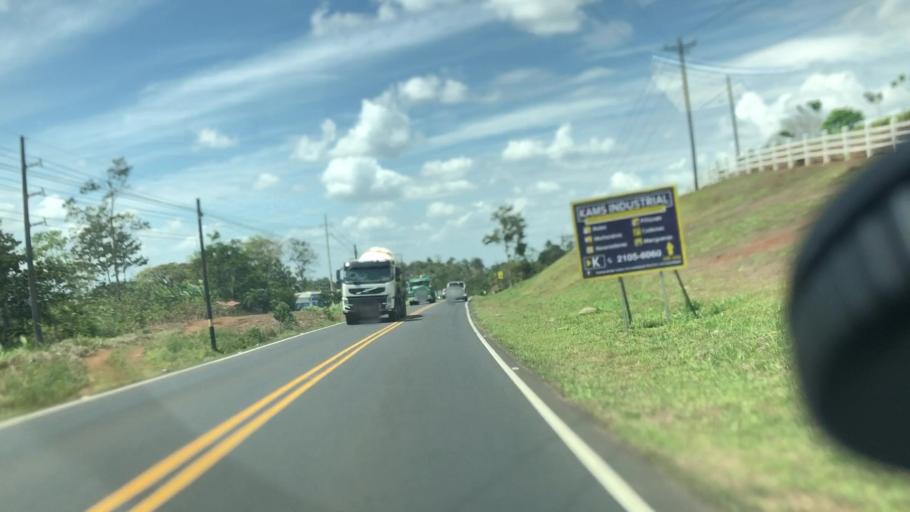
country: CR
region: Alajuela
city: Pital
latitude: 10.4559
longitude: -84.3856
